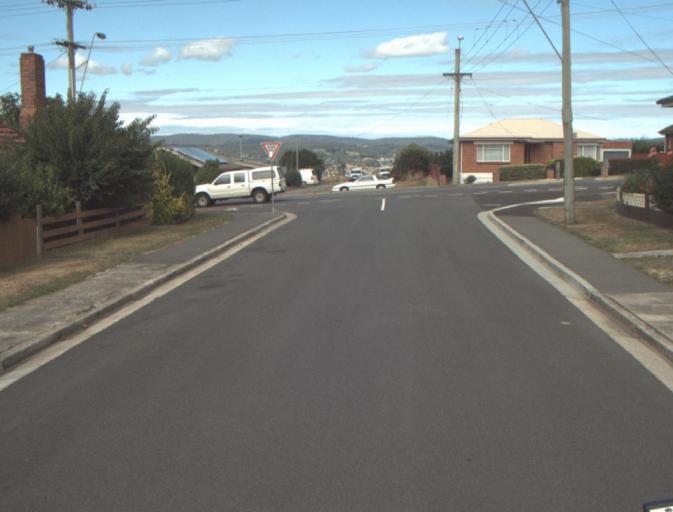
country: AU
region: Tasmania
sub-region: Launceston
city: Mayfield
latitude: -41.3794
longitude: 147.1281
